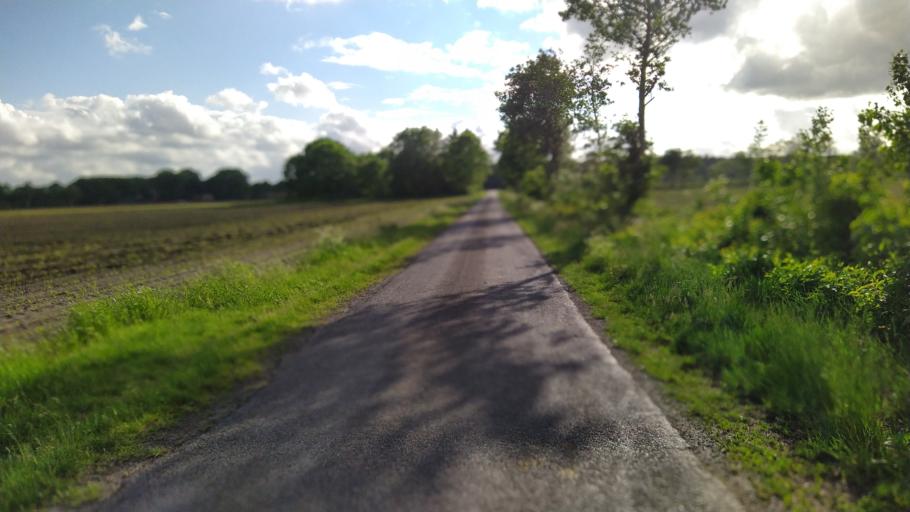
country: DE
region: Lower Saxony
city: Farven
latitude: 53.4425
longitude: 9.3088
